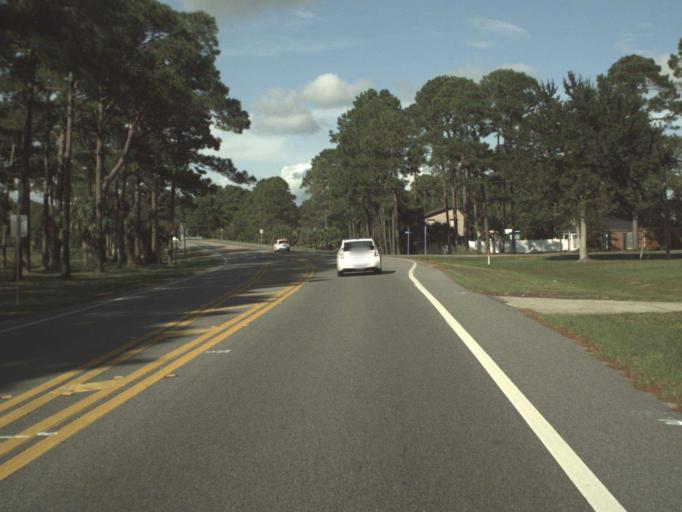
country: US
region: Florida
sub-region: Gulf County
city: Port Saint Joe
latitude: 29.7957
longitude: -85.3011
